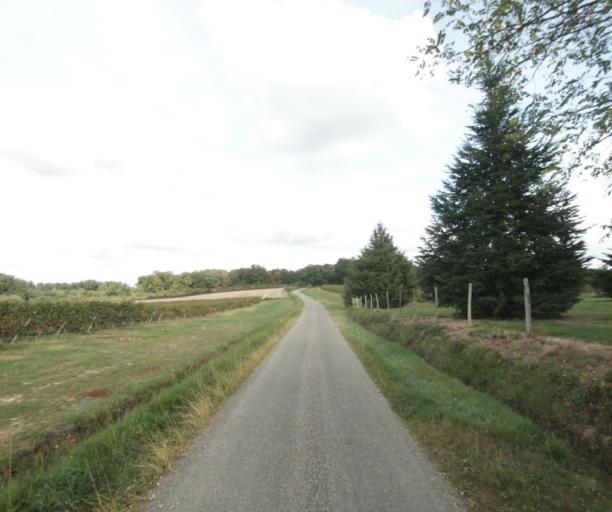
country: FR
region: Midi-Pyrenees
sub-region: Departement du Gers
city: Eauze
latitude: 43.8267
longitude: 0.1615
